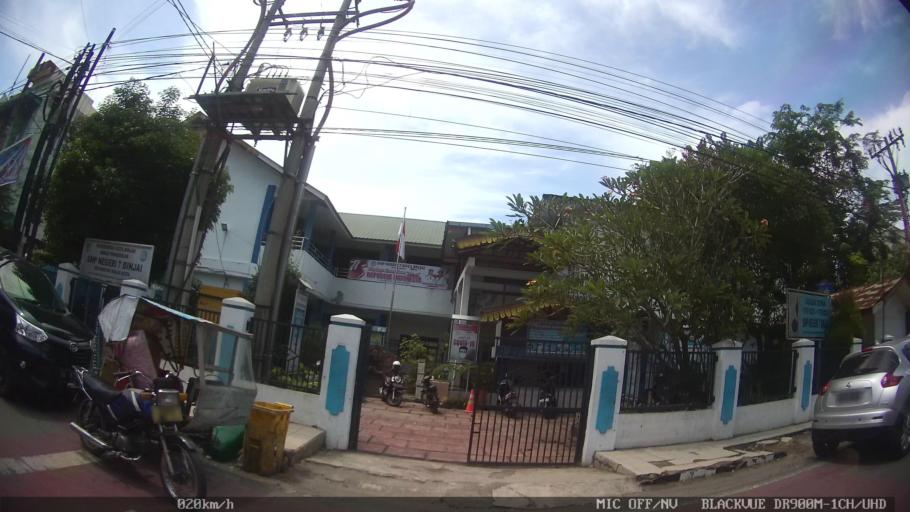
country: ID
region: North Sumatra
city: Binjai
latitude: 3.6017
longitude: 98.4828
